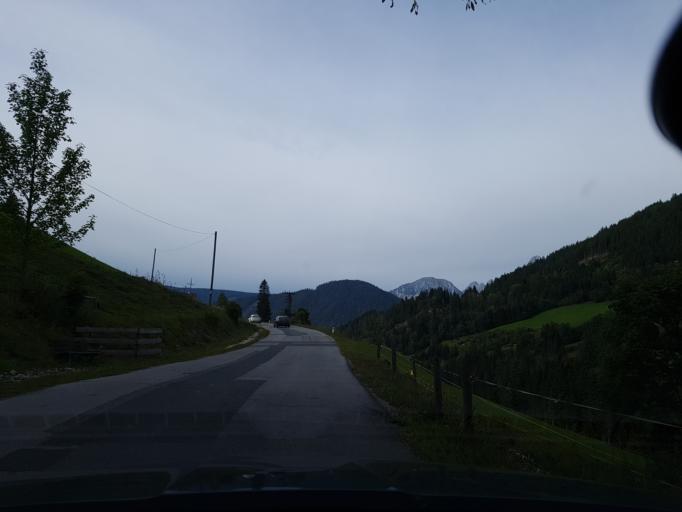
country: AT
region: Salzburg
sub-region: Politischer Bezirk Sankt Johann im Pongau
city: Forstau
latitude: 47.3603
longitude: 13.5617
